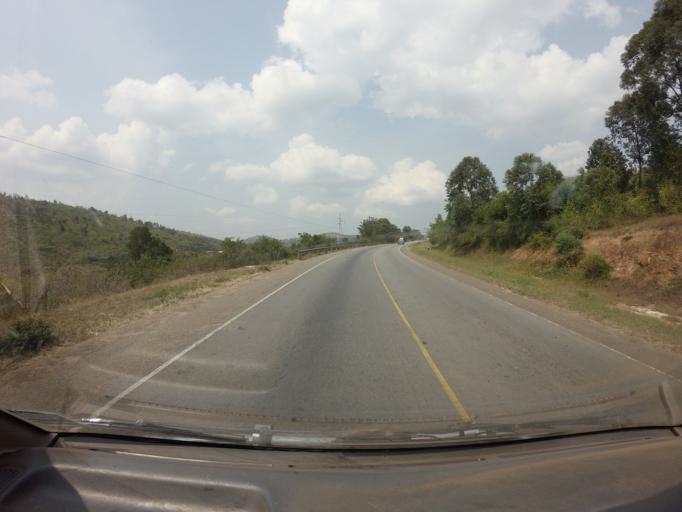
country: UG
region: Central Region
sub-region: Lyantonde District
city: Lyantonde
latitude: -0.3686
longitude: 31.2615
